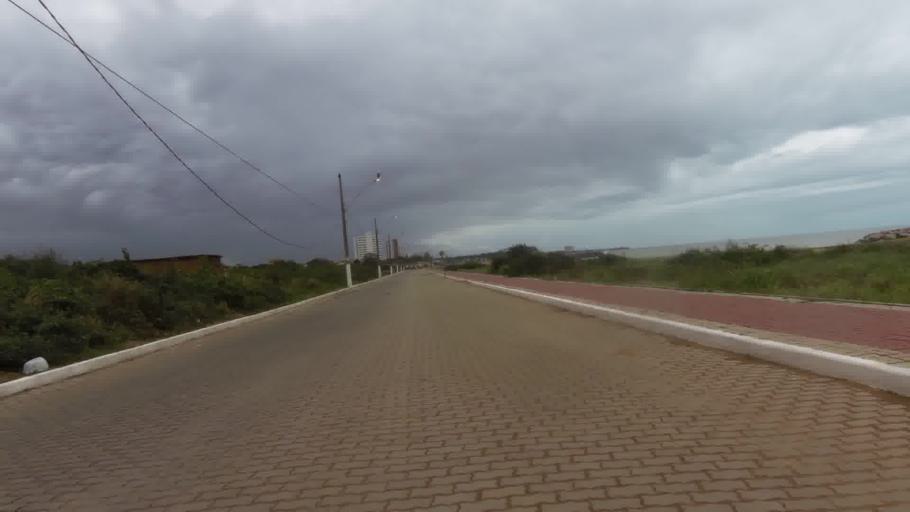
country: BR
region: Espirito Santo
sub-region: Marataizes
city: Marataizes
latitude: -21.0615
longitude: -40.8347
